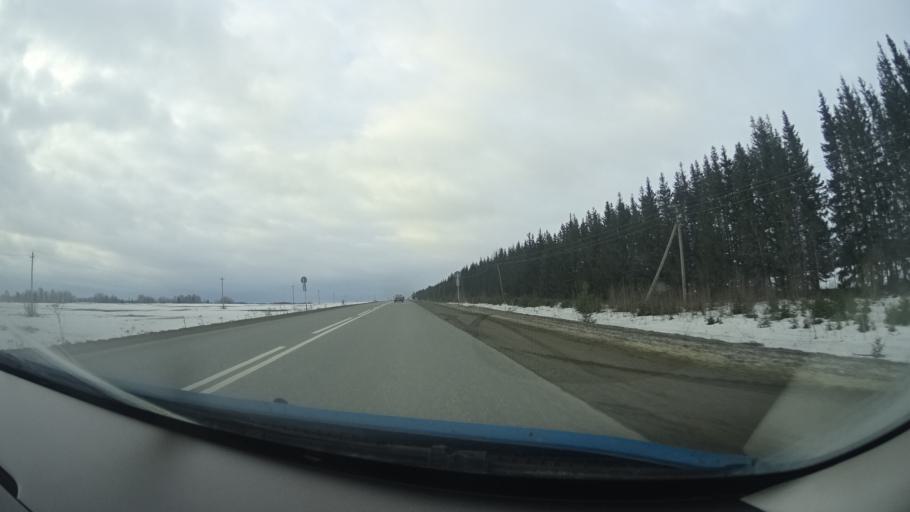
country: RU
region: Perm
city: Osa
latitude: 57.2748
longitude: 55.5687
